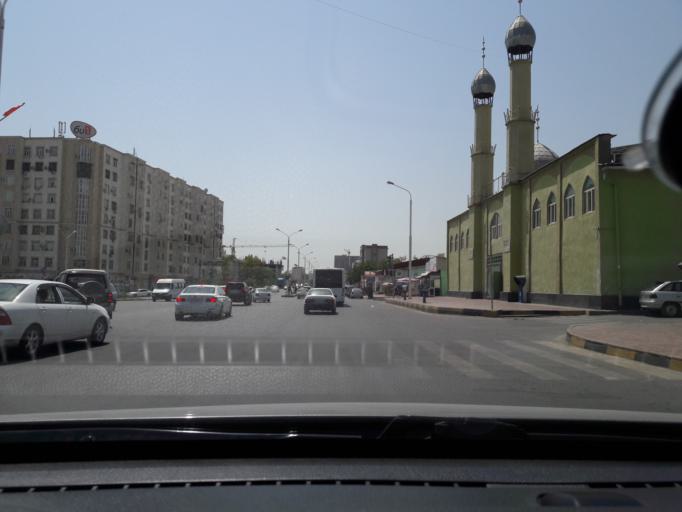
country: TJ
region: Dushanbe
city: Dushanbe
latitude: 38.5905
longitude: 68.7334
